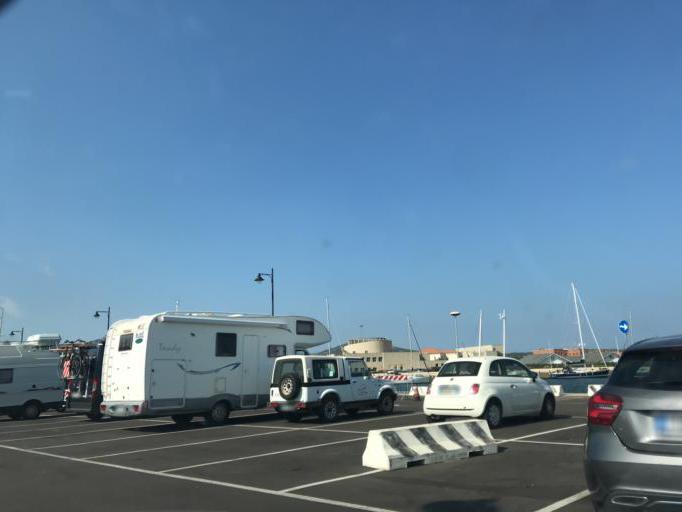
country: IT
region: Sardinia
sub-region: Provincia di Olbia-Tempio
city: Olbia
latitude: 40.9216
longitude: 9.5055
